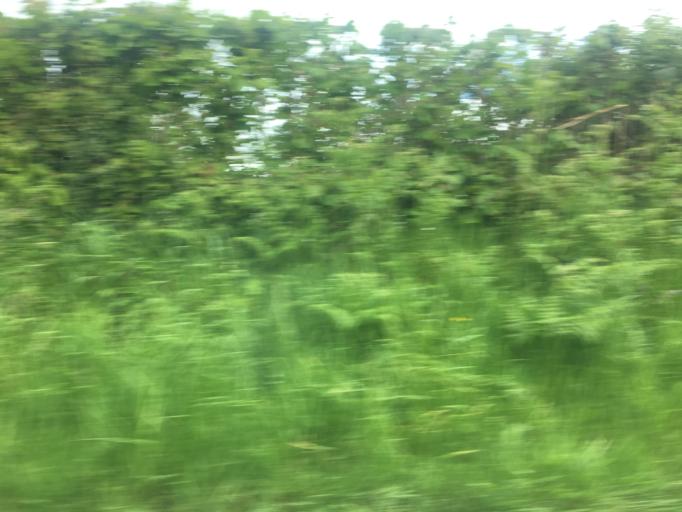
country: GB
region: Wales
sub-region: County of Ceredigion
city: Lampeter
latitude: 52.1311
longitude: -4.0733
